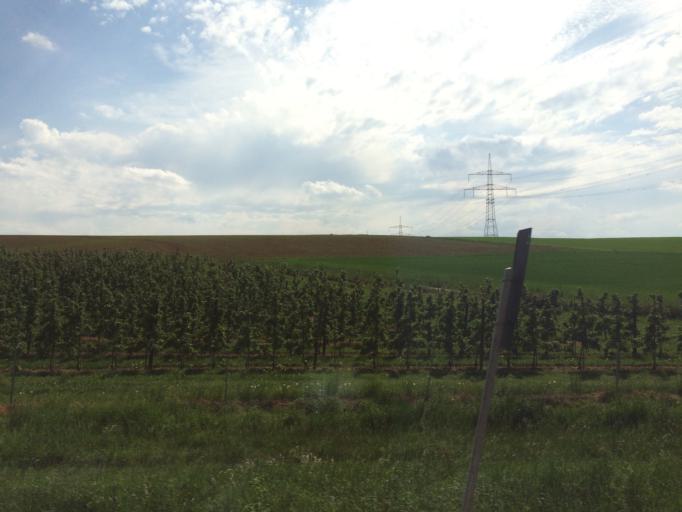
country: DE
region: Bavaria
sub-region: Regierungsbezirk Unterfranken
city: Biebelried
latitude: 49.8037
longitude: 10.0727
